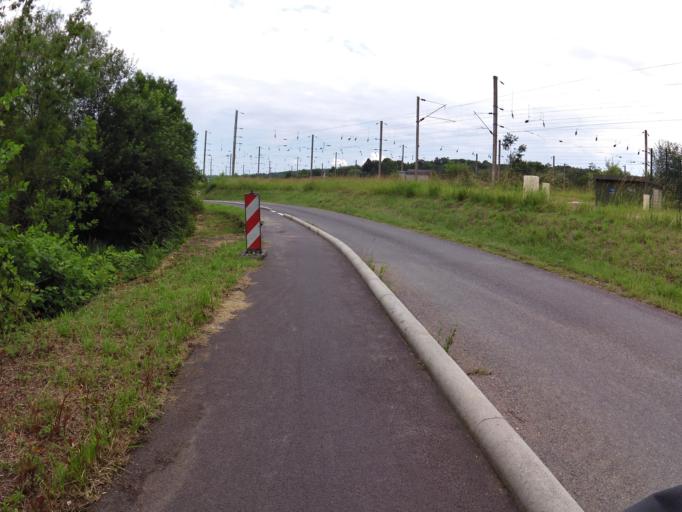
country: FR
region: Champagne-Ardenne
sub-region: Departement des Ardennes
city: Lumes
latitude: 49.7170
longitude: 4.7821
